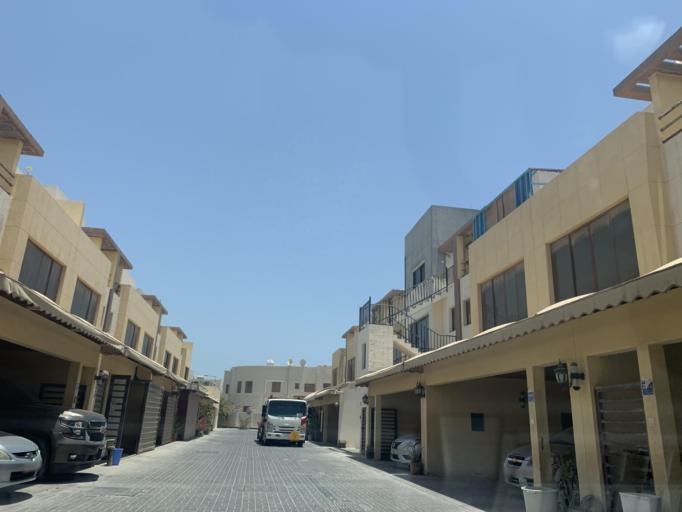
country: BH
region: Muharraq
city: Al Muharraq
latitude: 26.2840
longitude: 50.6190
